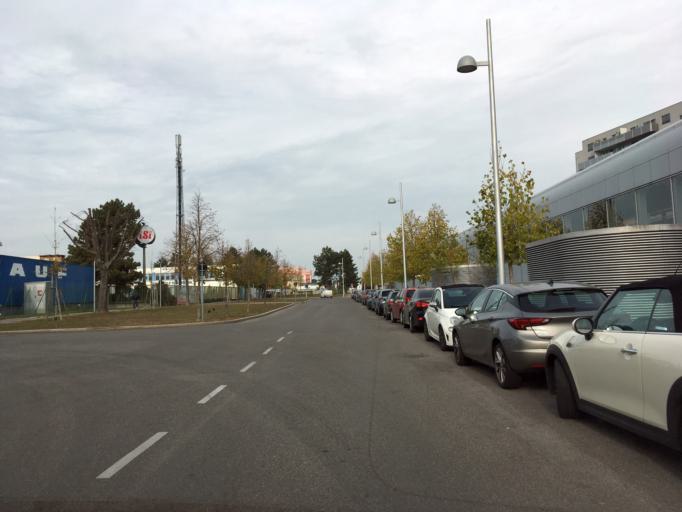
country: AT
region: Lower Austria
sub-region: Politischer Bezirk Wien-Umgebung
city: Gerasdorf bei Wien
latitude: 48.2630
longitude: 16.4513
